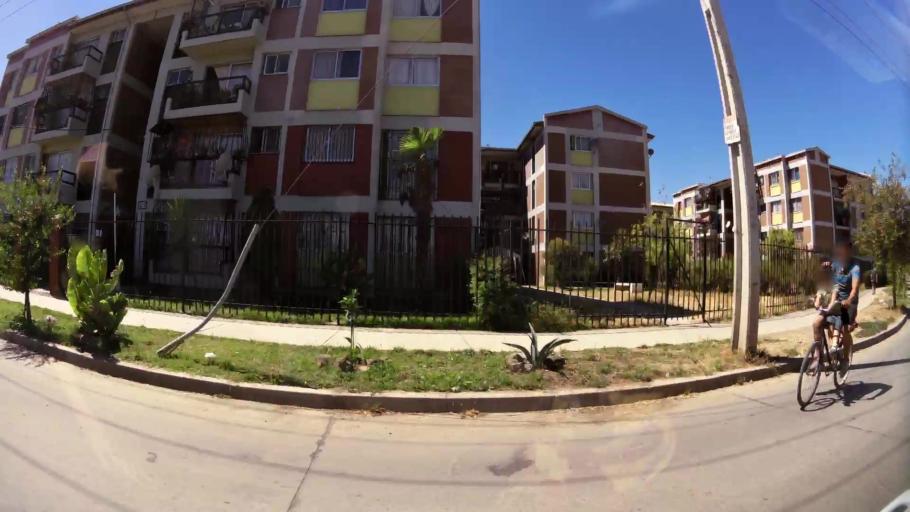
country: CL
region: O'Higgins
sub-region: Provincia de Cachapoal
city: Rancagua
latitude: -34.1553
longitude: -70.7223
